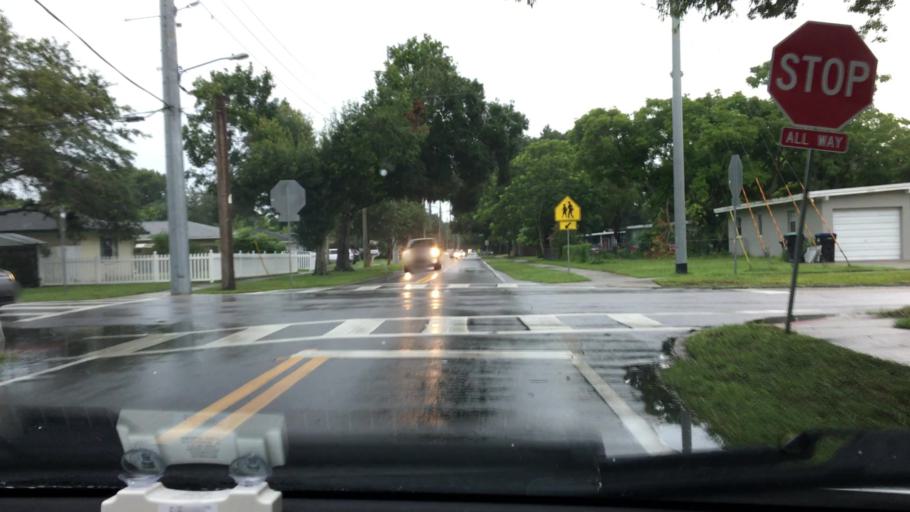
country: US
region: Florida
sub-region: Orange County
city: Conway
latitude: 28.5063
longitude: -81.3392
